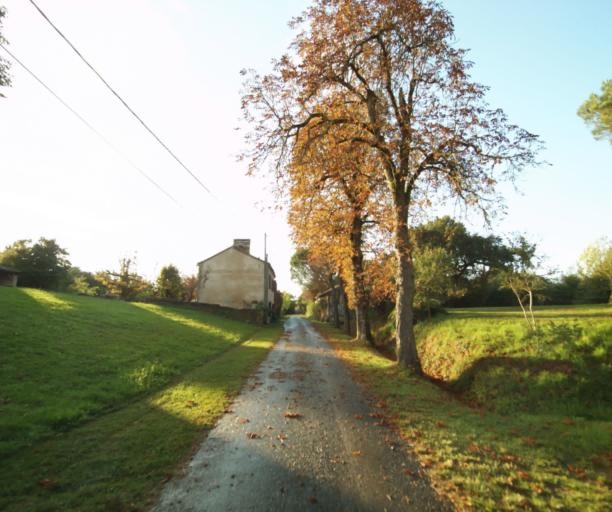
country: FR
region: Midi-Pyrenees
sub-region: Departement du Gers
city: Cazaubon
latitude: 43.9065
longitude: -0.0318
